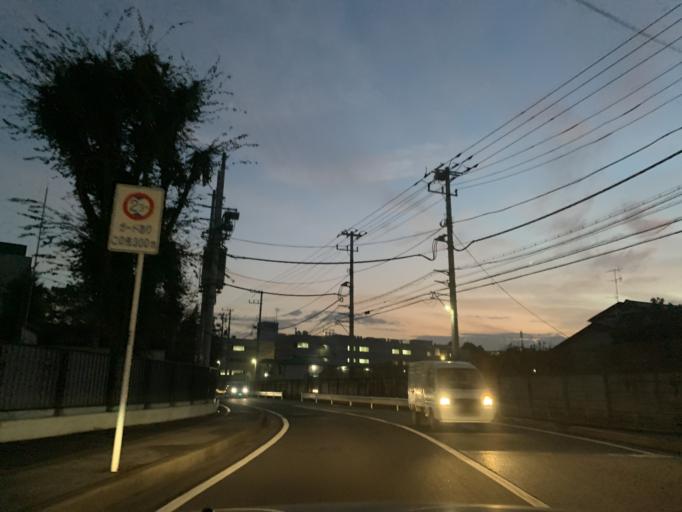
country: JP
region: Chiba
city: Noda
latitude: 35.9193
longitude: 139.9069
